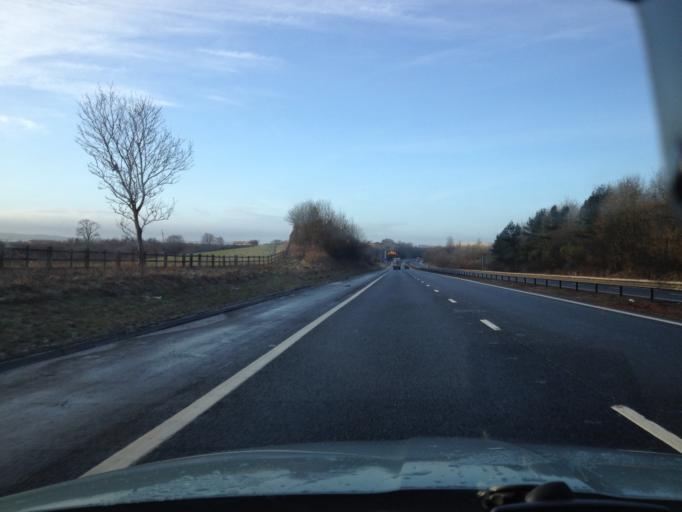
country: GB
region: Scotland
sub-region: West Lothian
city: Blackburn
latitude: 55.8851
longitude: -3.6142
